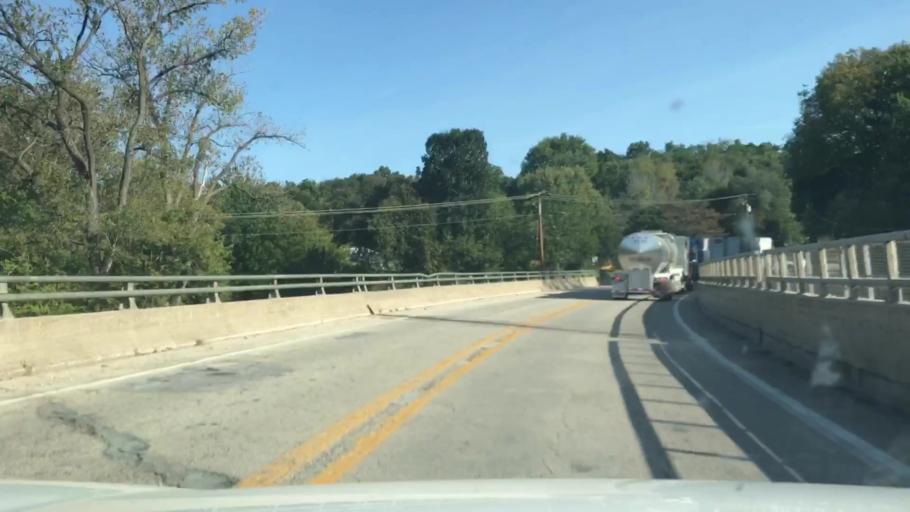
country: US
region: Illinois
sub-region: Adams County
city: Quincy
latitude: 39.8413
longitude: -91.3696
